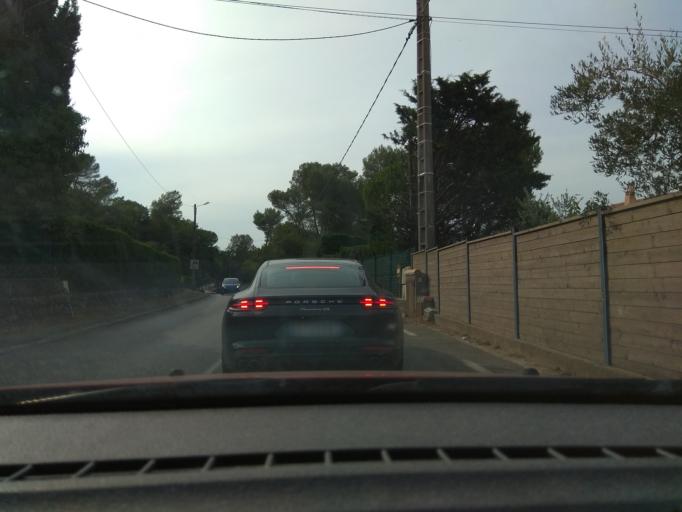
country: FR
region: Provence-Alpes-Cote d'Azur
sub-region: Departement des Alpes-Maritimes
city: Valbonne
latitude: 43.6428
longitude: 7.0251
